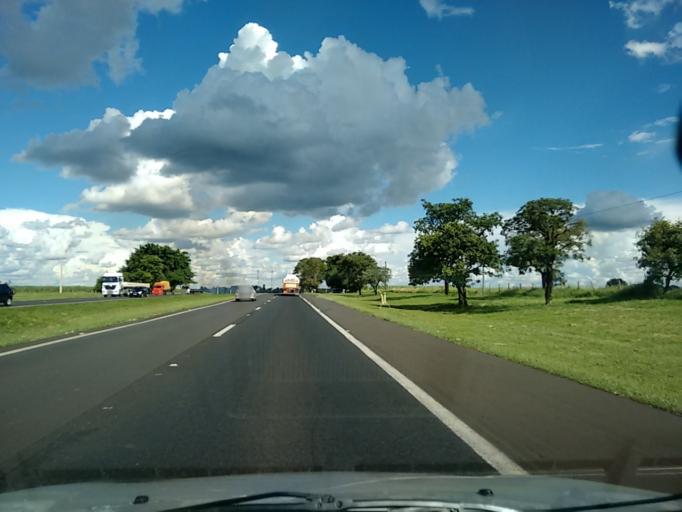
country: BR
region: Sao Paulo
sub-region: Ibate
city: Ibate
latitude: -21.9026
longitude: -48.0595
